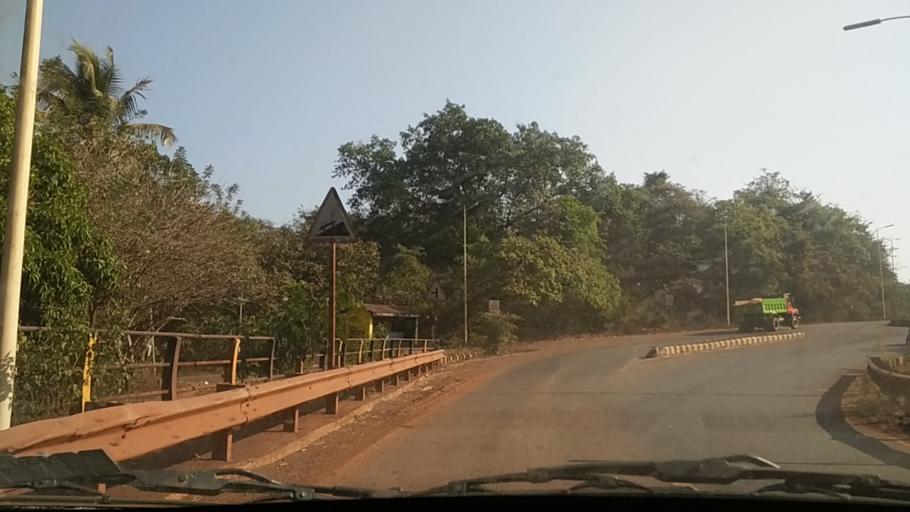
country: IN
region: Goa
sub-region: South Goa
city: Sanvordem
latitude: 15.3584
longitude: 74.1270
